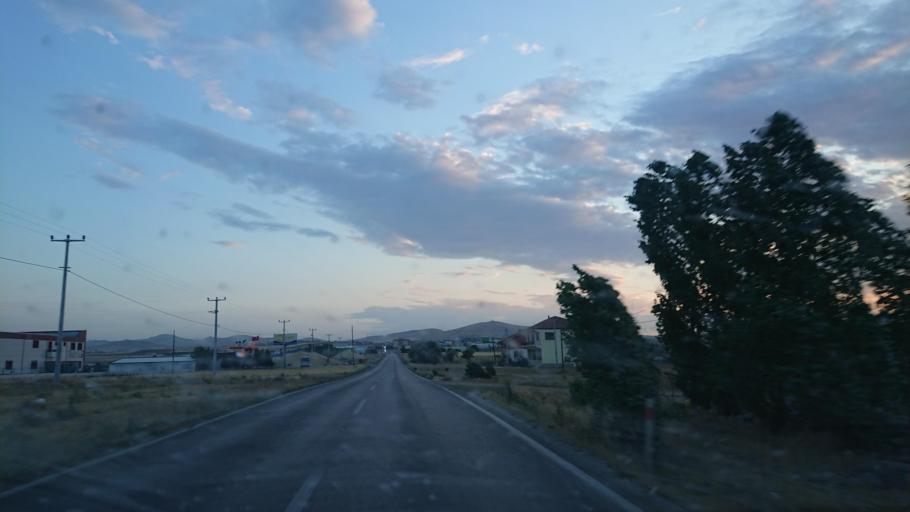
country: TR
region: Aksaray
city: Balci
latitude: 38.7613
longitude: 34.0860
